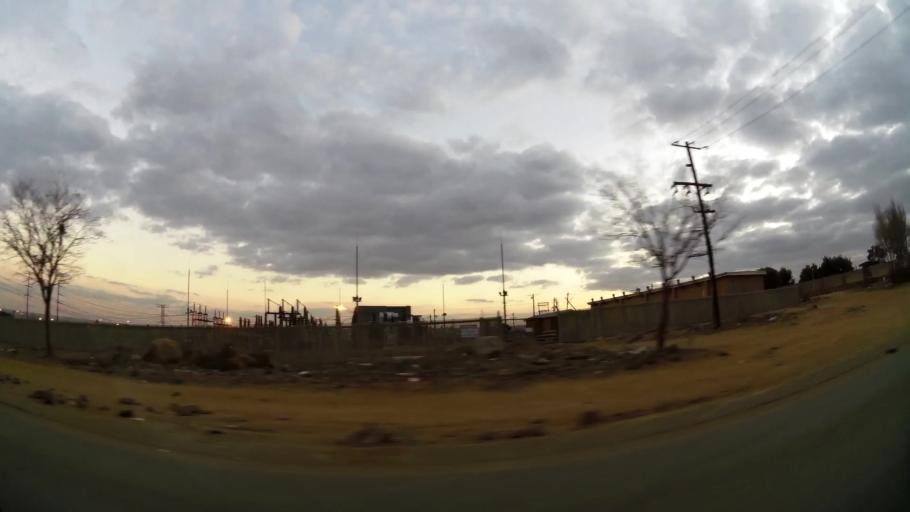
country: ZA
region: Gauteng
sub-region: Ekurhuleni Metropolitan Municipality
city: Tembisa
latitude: -25.9978
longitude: 28.1882
